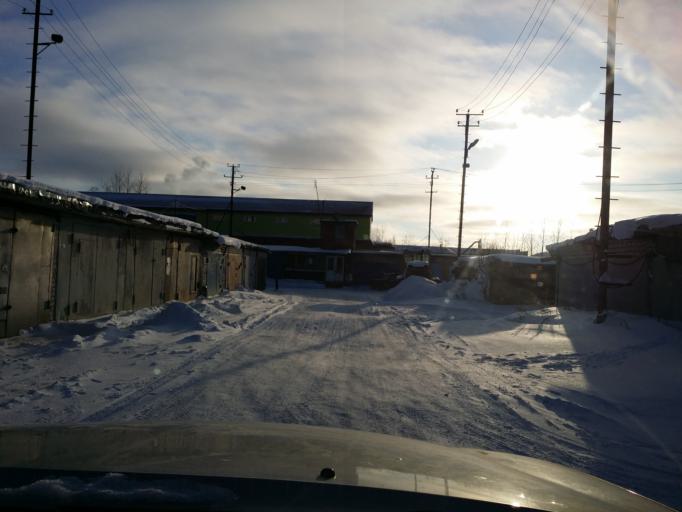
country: RU
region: Khanty-Mansiyskiy Avtonomnyy Okrug
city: Megion
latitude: 61.0441
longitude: 76.1021
